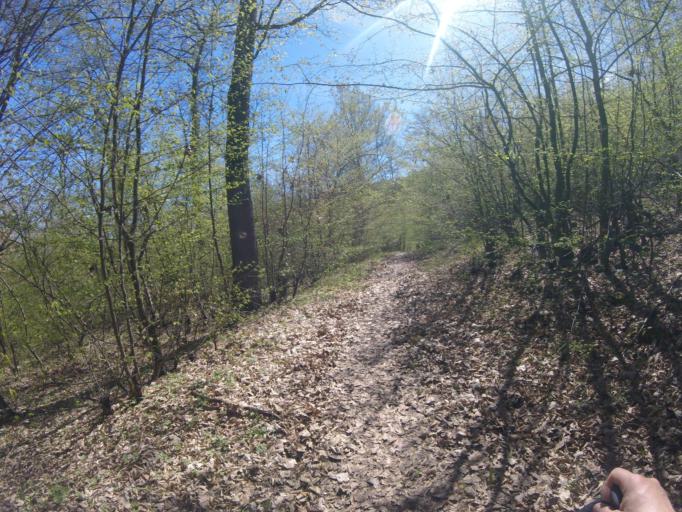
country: HU
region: Borsod-Abauj-Zemplen
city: Szendro
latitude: 48.4085
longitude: 20.7629
